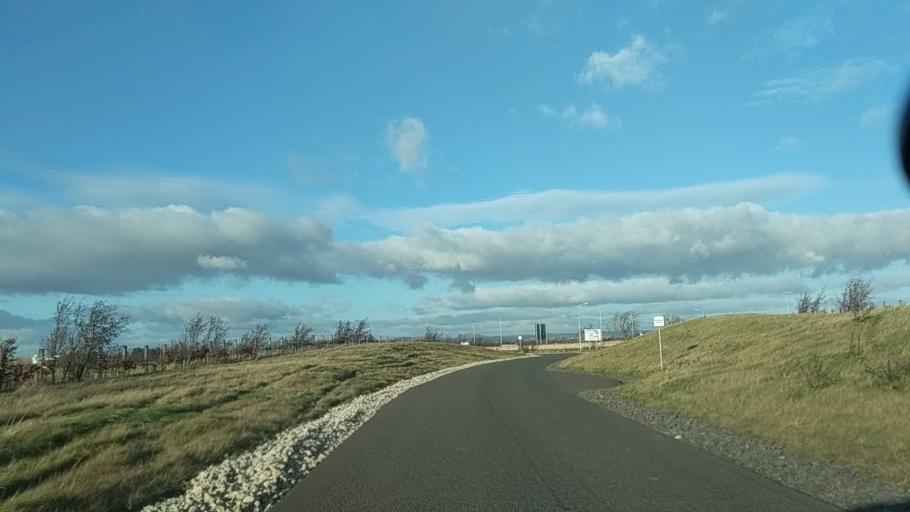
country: GB
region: Scotland
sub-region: Edinburgh
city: Queensferry
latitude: 55.9830
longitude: -3.4252
